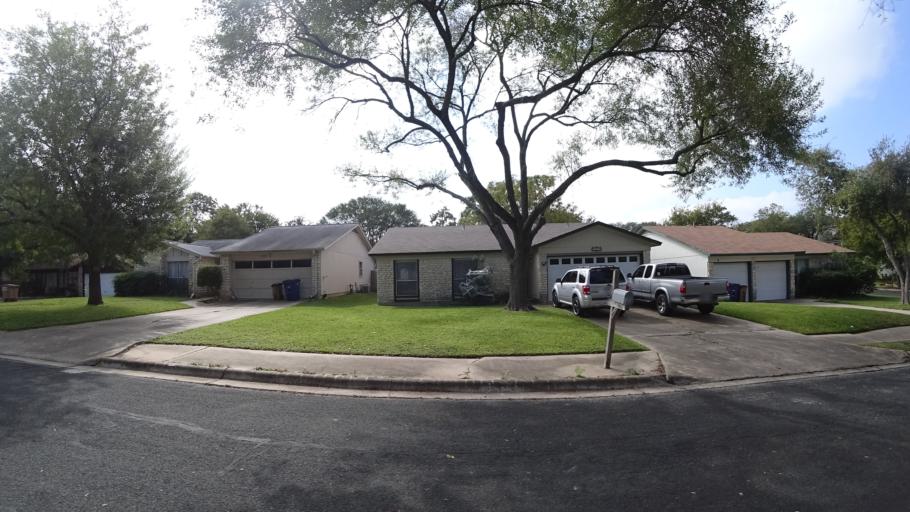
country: US
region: Texas
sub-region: Travis County
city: Shady Hollow
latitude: 30.2009
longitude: -97.8295
